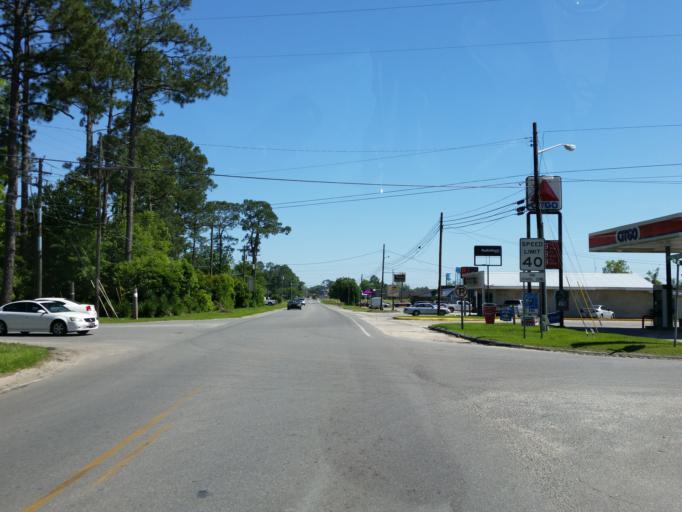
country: US
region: Georgia
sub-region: Cook County
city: Adel
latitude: 31.1483
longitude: -83.4274
